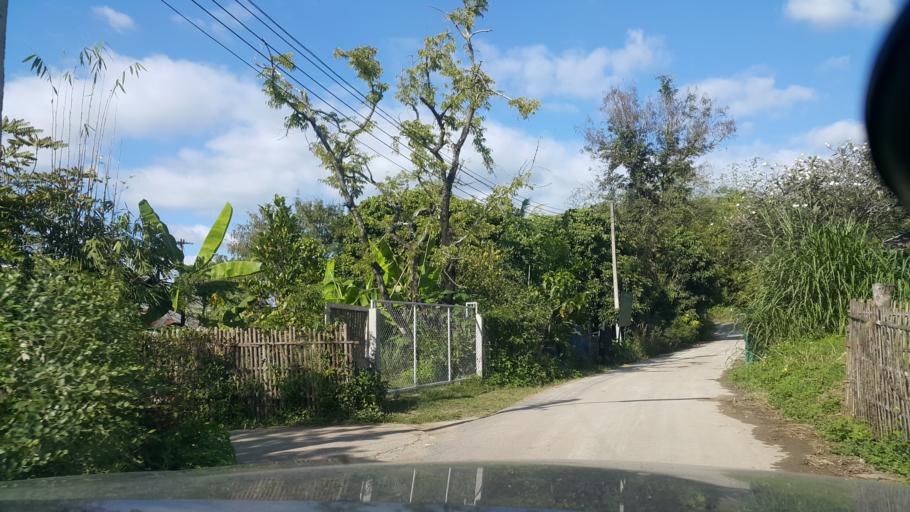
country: TH
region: Chiang Mai
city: Mae On
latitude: 18.7730
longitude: 99.2592
